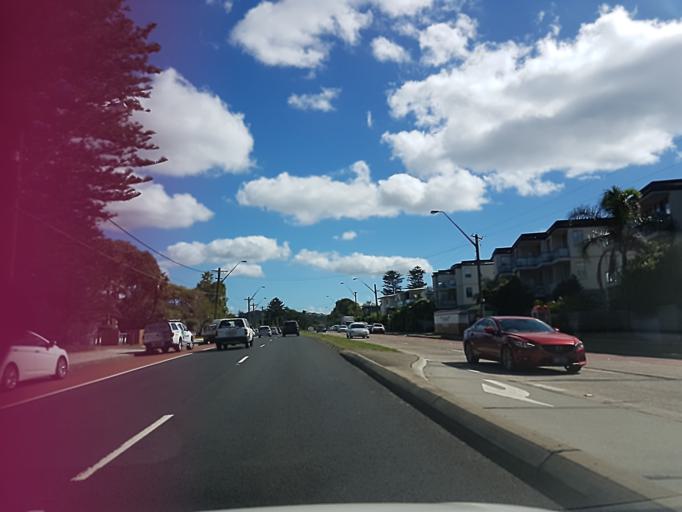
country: AU
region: New South Wales
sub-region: Warringah
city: Narrabeen
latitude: -33.7184
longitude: 151.2977
